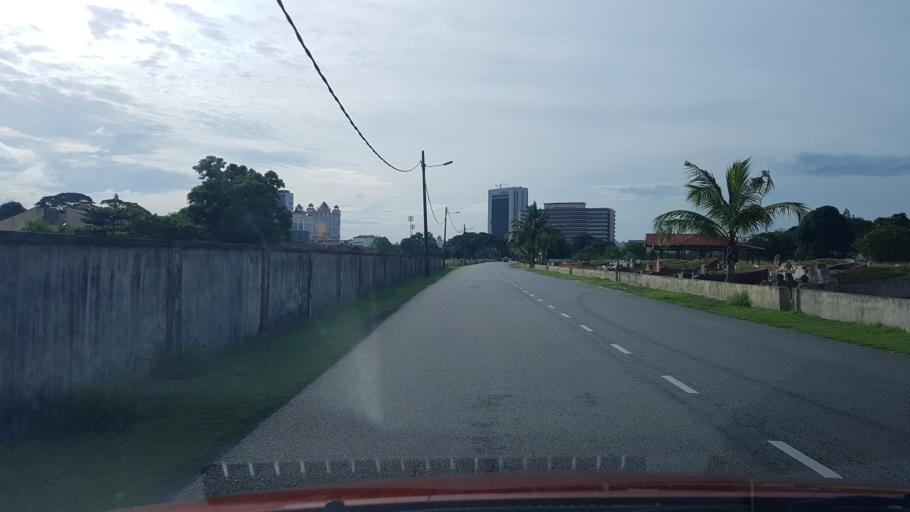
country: MY
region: Terengganu
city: Kuala Terengganu
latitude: 5.3232
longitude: 103.1452
